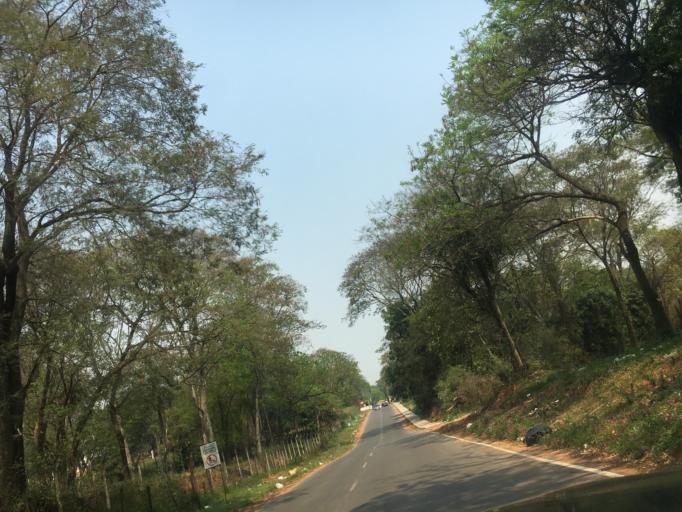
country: PY
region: Central
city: Villa Elisa
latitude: -25.3772
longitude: -57.5907
